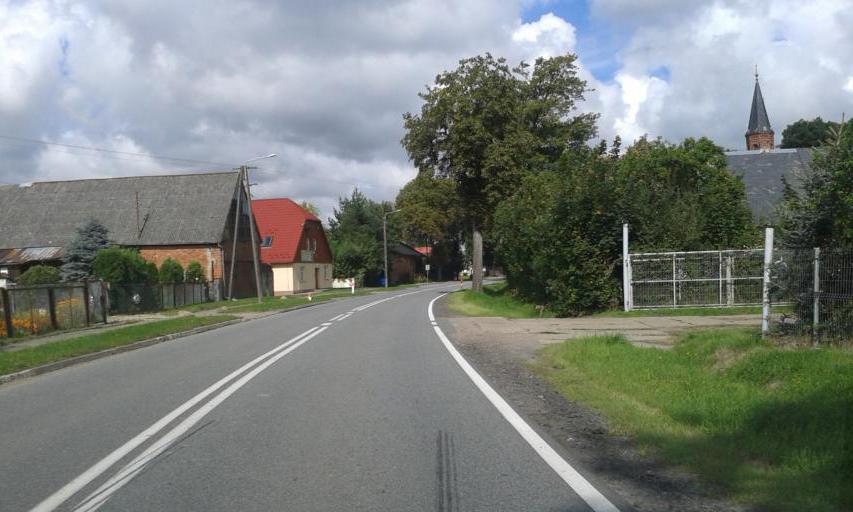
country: PL
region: West Pomeranian Voivodeship
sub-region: Powiat slawienski
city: Darlowo
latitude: 54.3572
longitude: 16.5166
